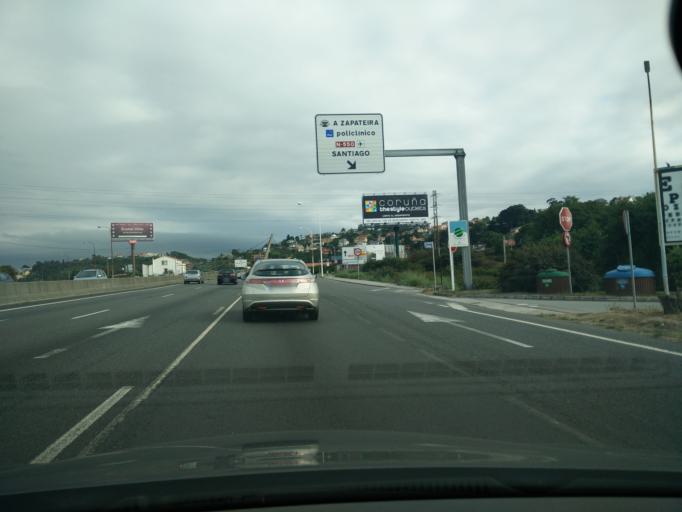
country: ES
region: Galicia
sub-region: Provincia da Coruna
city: A Coruna
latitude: 43.3335
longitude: -8.4020
